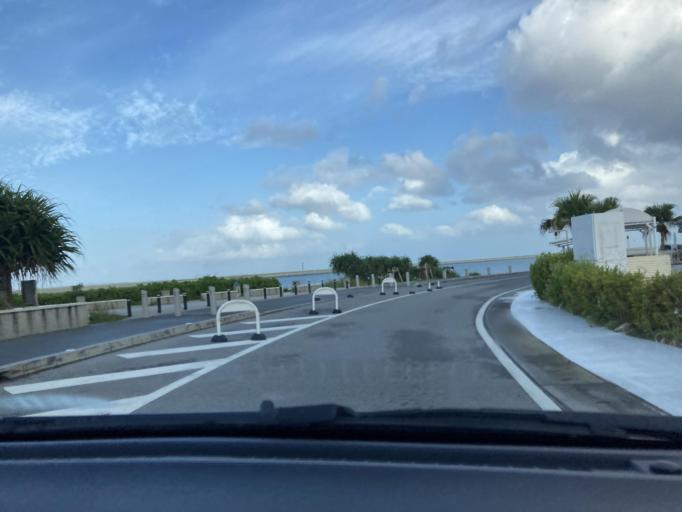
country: JP
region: Okinawa
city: Tomigusuku
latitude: 26.1760
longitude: 127.6404
